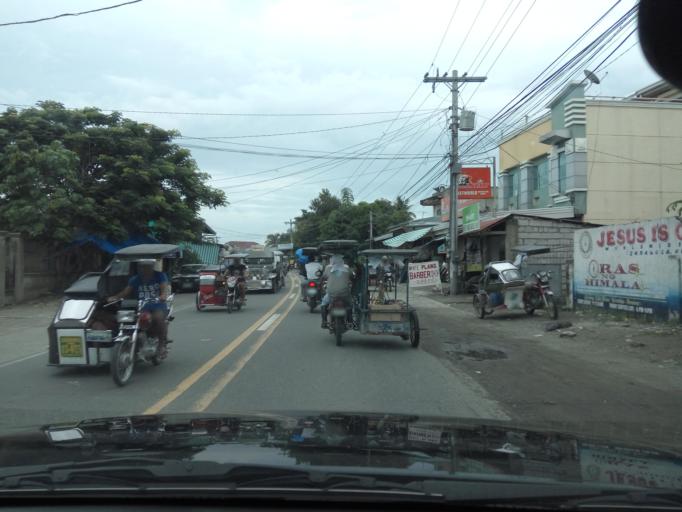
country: PH
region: Central Luzon
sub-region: Province of Nueva Ecija
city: Concepcion
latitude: 15.4491
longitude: 120.7939
